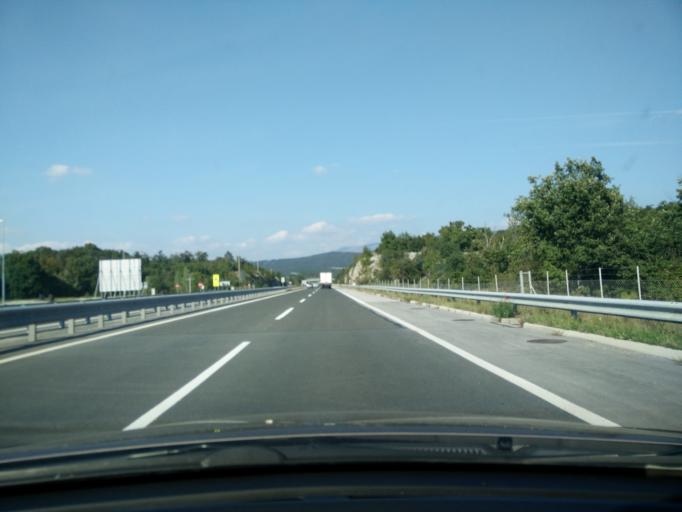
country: SI
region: Divaca
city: Divaca
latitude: 45.6724
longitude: 13.9711
